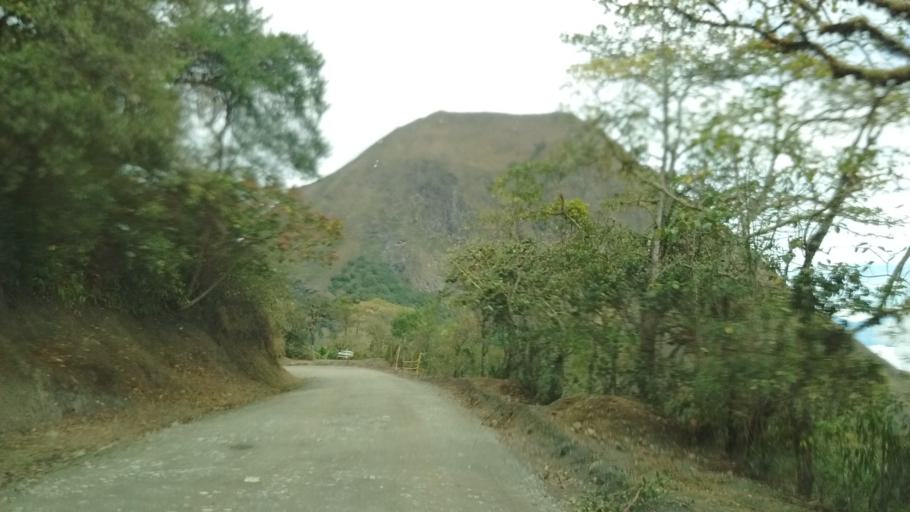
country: CO
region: Cauca
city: Almaguer
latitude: 1.8564
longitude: -76.9440
